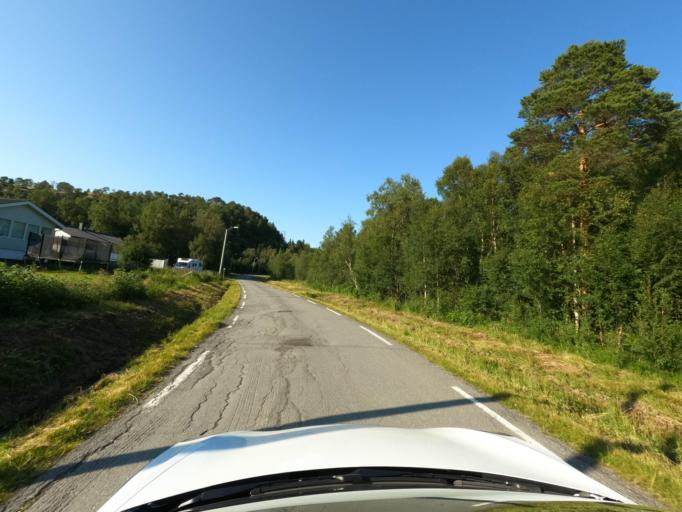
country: NO
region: Nordland
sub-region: Narvik
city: Narvik
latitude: 68.4734
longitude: 17.5088
